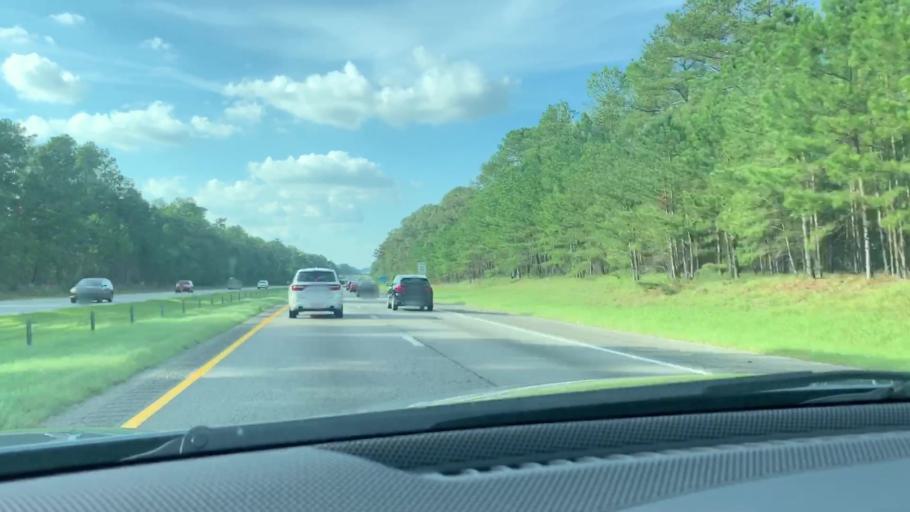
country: US
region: South Carolina
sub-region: Orangeburg County
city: Brookdale
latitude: 33.5263
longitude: -80.7973
